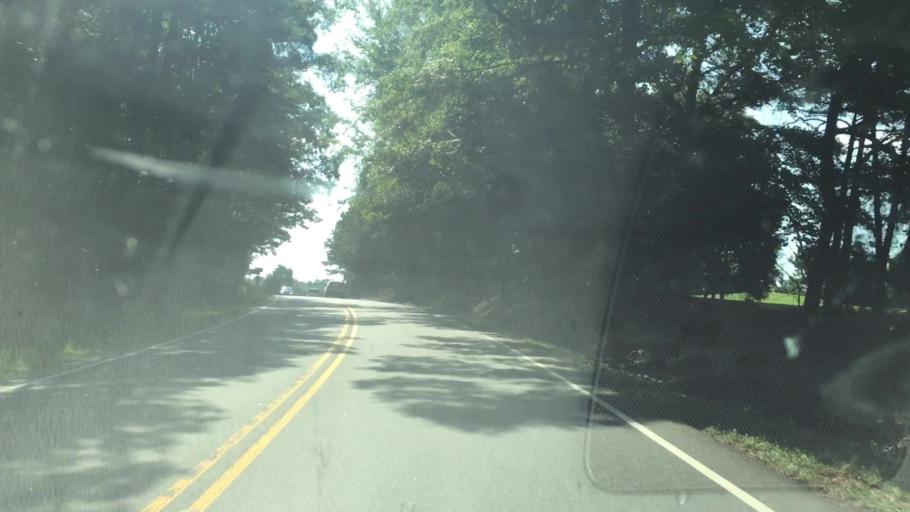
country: US
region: North Carolina
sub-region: Mecklenburg County
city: Mint Hill
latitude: 35.1687
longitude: -80.5998
